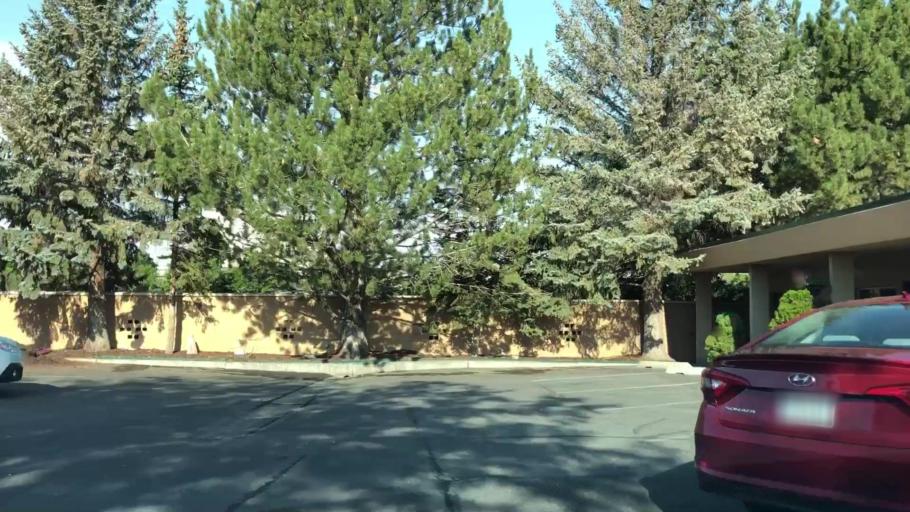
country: US
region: Idaho
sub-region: Bonneville County
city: Idaho Falls
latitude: 43.4978
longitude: -112.0444
